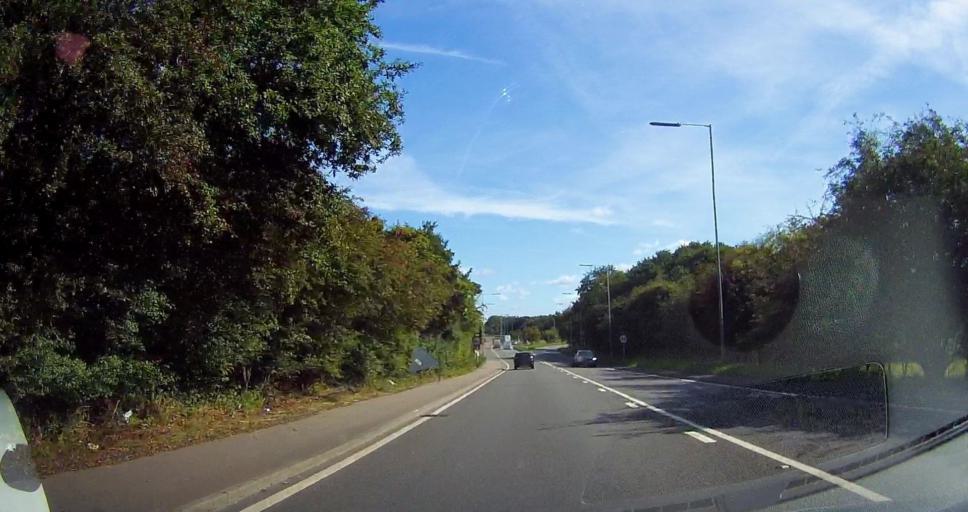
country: GB
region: England
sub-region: Staffordshire
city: Norton Canes
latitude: 52.6563
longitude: -1.9559
